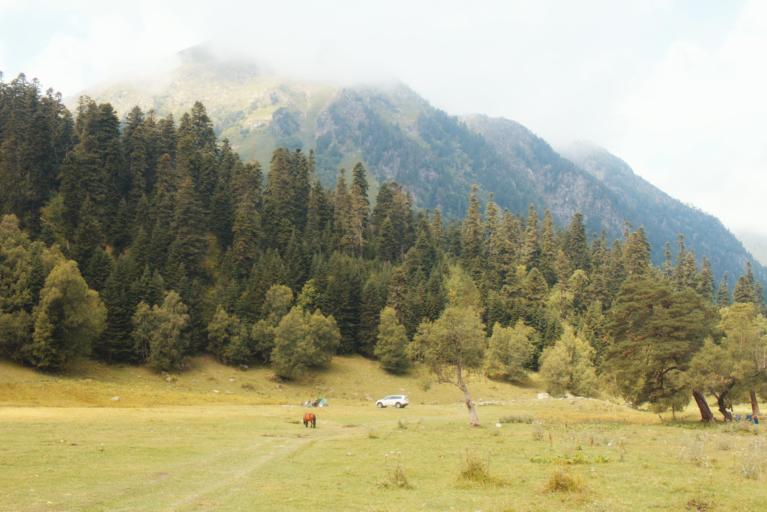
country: RU
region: Karachayevo-Cherkesiya
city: Nizhniy Arkhyz
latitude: 43.4514
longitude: 41.2716
